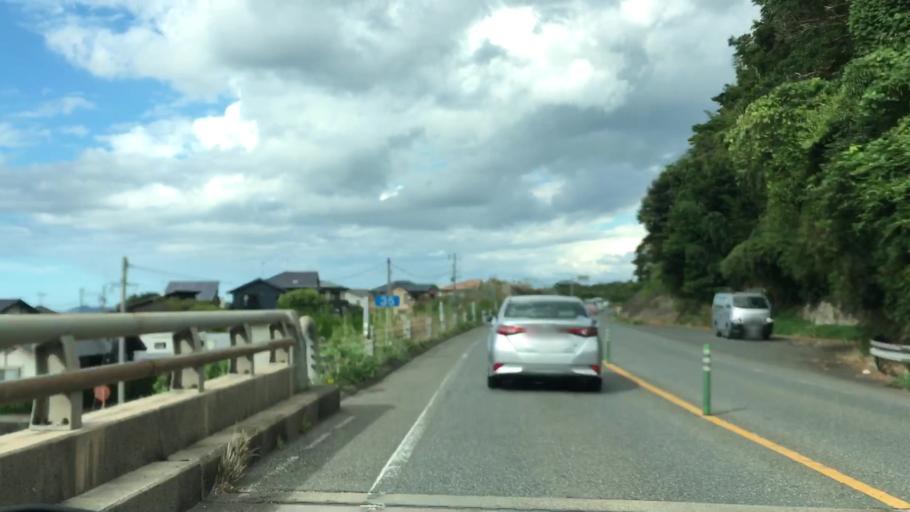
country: JP
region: Saga Prefecture
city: Karatsu
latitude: 33.4988
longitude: 130.0817
